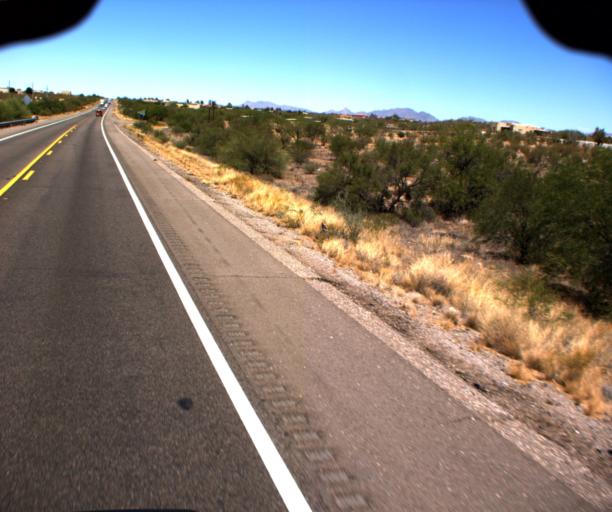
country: US
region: Arizona
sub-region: Maricopa County
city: Wickenburg
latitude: 34.0323
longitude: -112.8196
